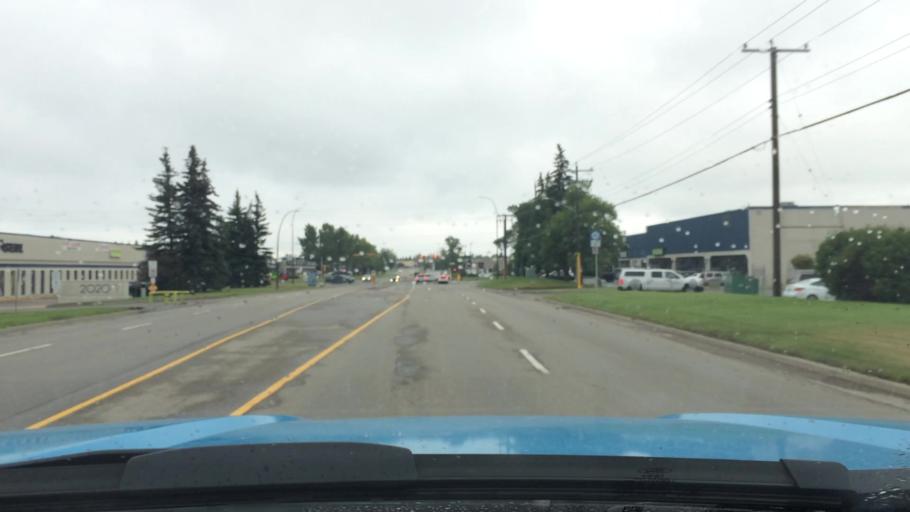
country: CA
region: Alberta
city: Calgary
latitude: 51.0832
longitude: -114.0117
